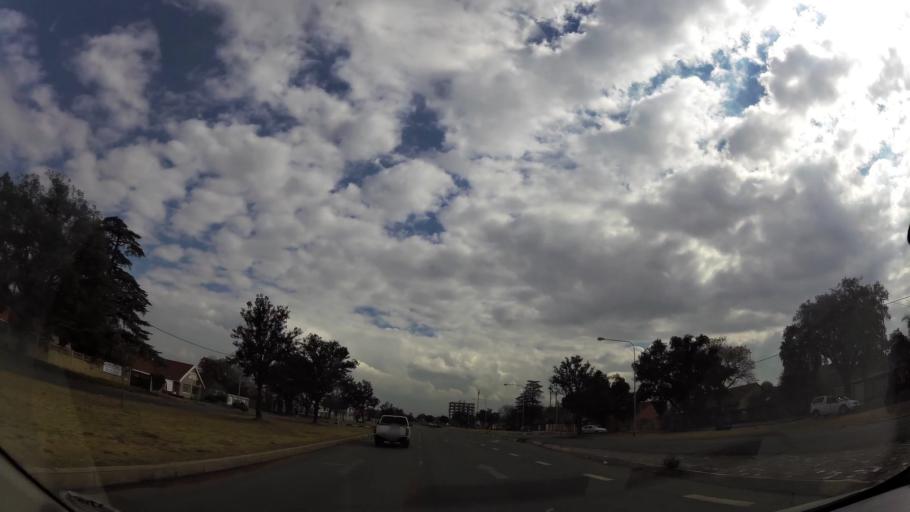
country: ZA
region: Gauteng
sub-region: Sedibeng District Municipality
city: Vereeniging
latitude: -26.6608
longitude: 27.9746
